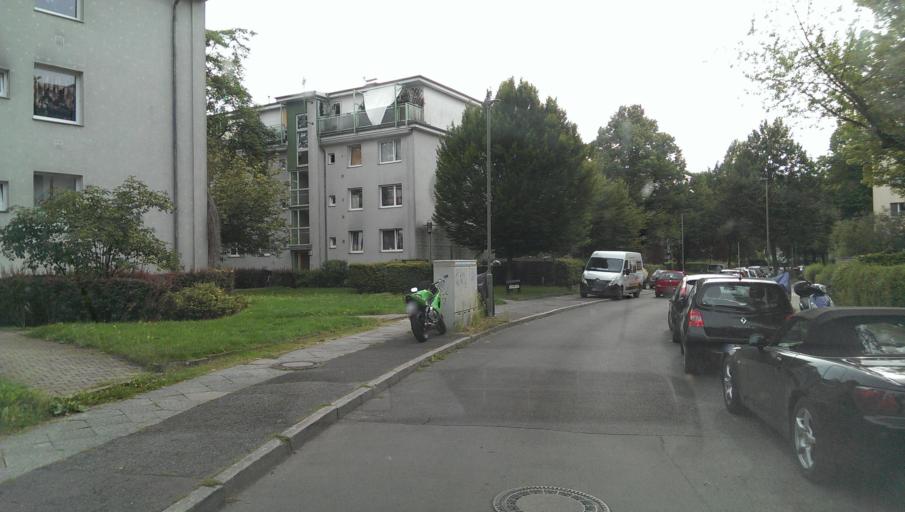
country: DE
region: Brandenburg
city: Teltow
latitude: 52.4103
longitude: 13.2552
